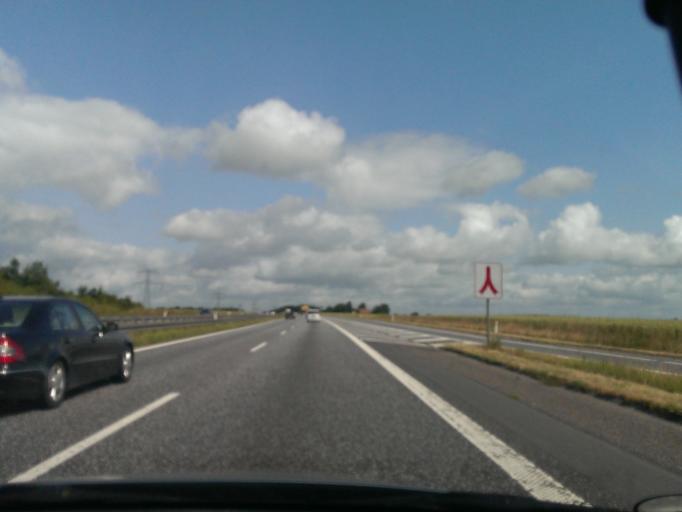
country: DK
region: Central Jutland
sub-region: Randers Kommune
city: Randers
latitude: 56.4927
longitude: 9.9801
